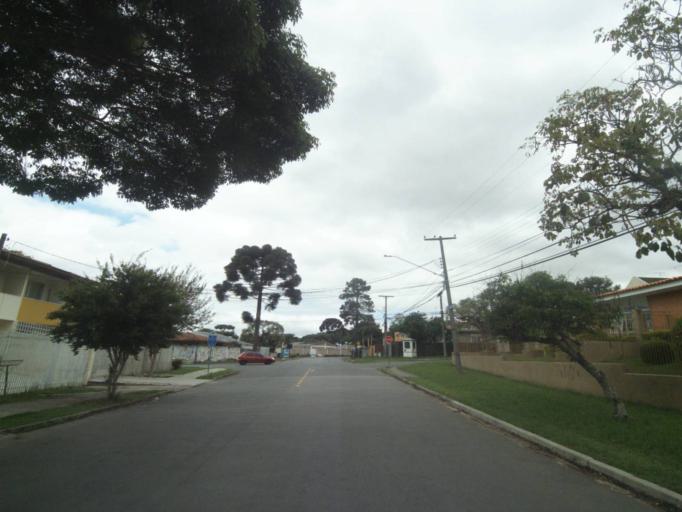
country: BR
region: Parana
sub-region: Pinhais
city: Pinhais
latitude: -25.4085
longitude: -49.2242
